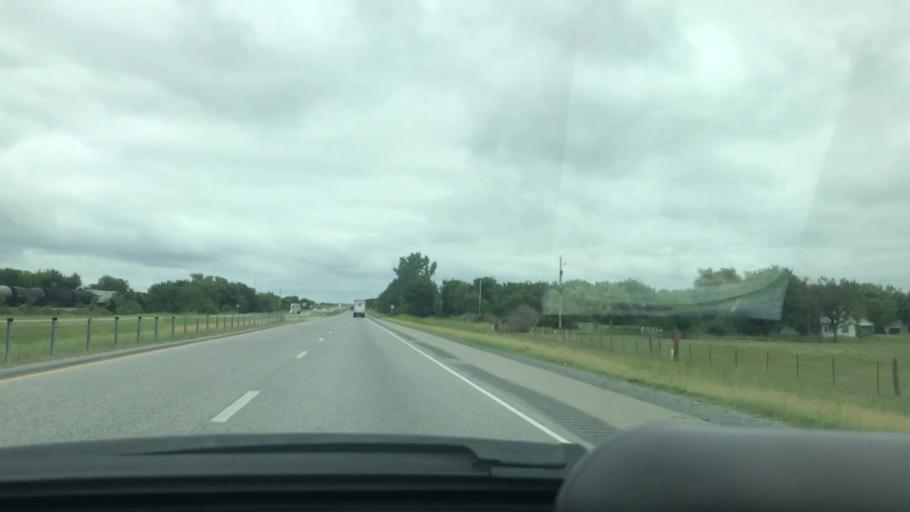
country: US
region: Oklahoma
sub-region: Pittsburg County
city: McAlester
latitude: 34.7395
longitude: -95.8983
